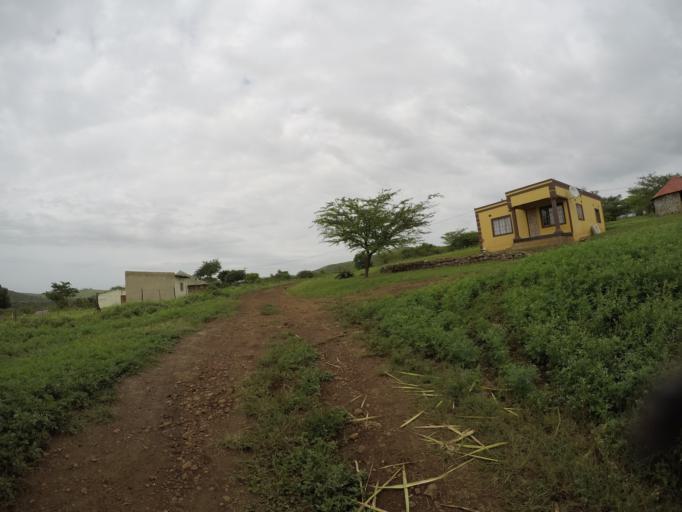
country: ZA
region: KwaZulu-Natal
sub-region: uThungulu District Municipality
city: Empangeni
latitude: -28.6406
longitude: 31.9074
